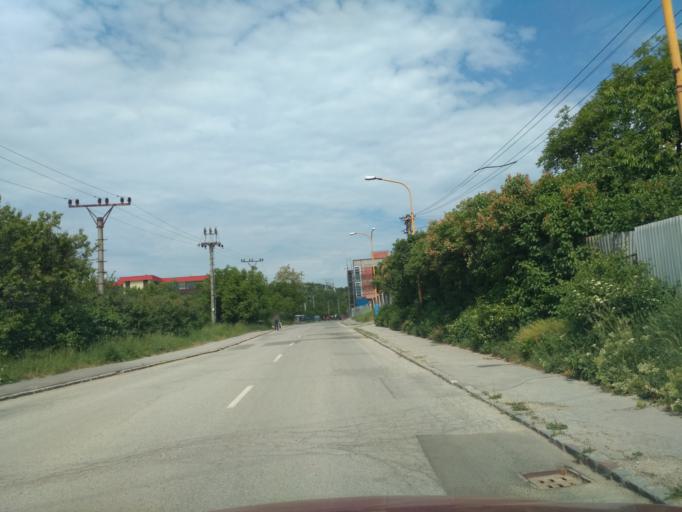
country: SK
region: Kosicky
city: Kosice
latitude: 48.7311
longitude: 21.2305
